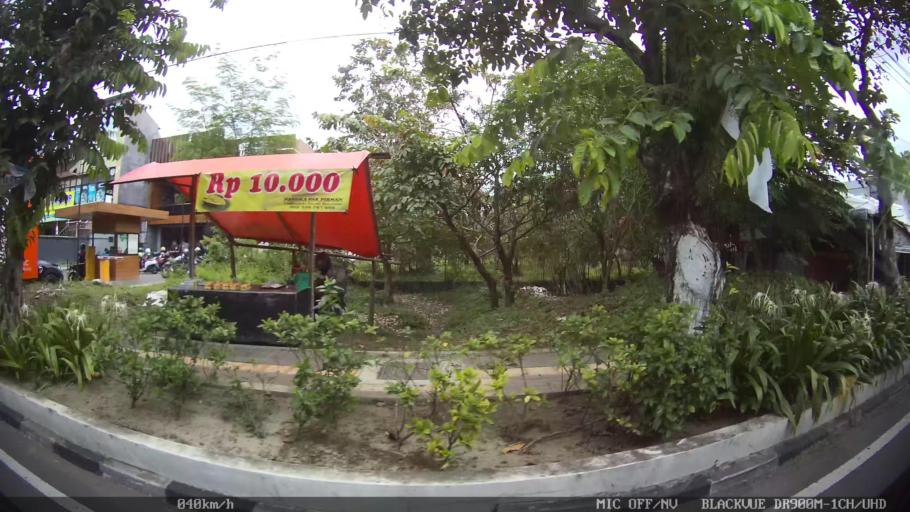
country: ID
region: Daerah Istimewa Yogyakarta
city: Yogyakarta
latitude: -7.7949
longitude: 110.3928
